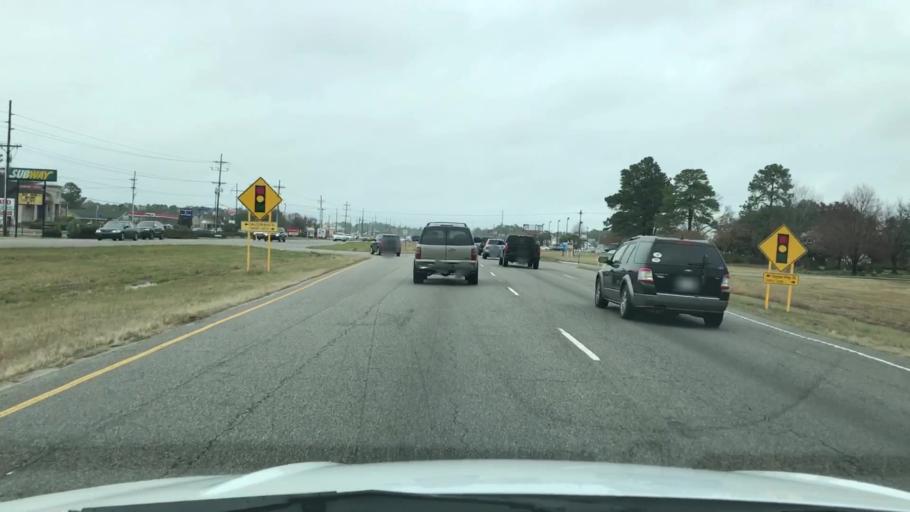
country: US
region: South Carolina
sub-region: Horry County
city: Red Hill
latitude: 33.7880
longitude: -78.9944
